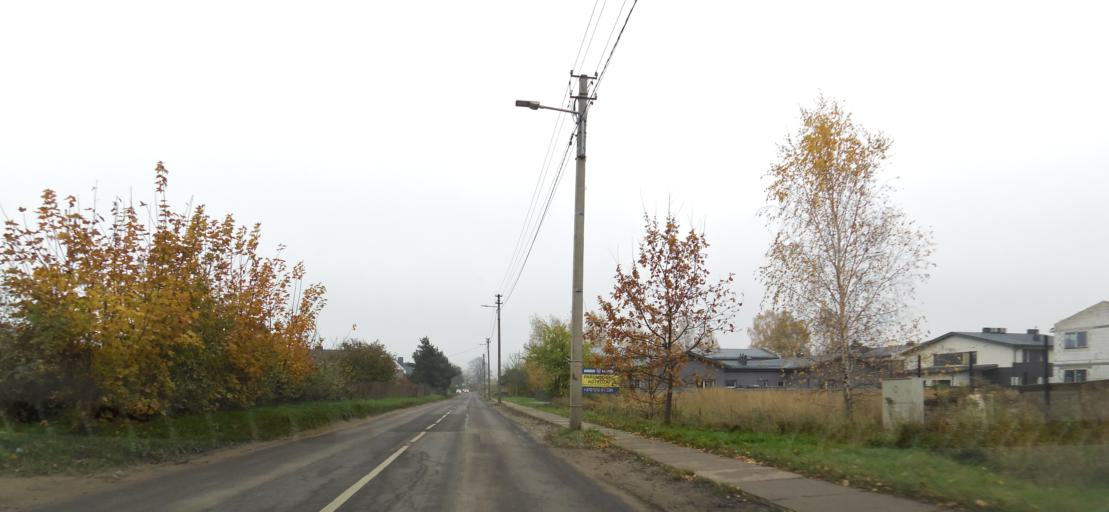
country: LT
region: Vilnius County
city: Rasos
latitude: 54.6609
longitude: 25.3518
